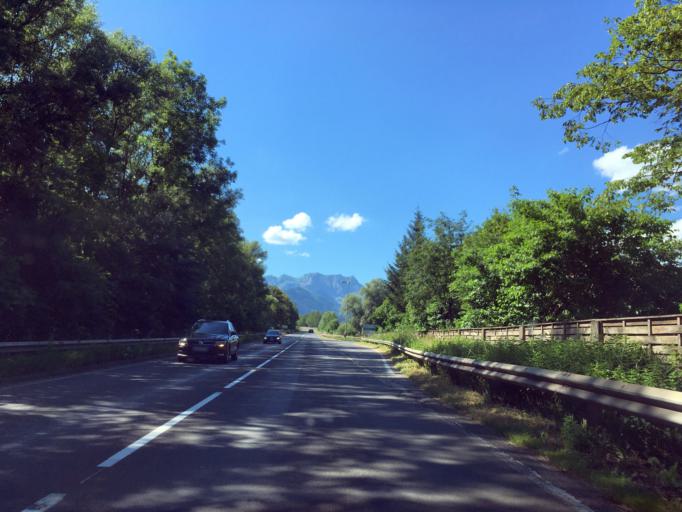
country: AT
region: Styria
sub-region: Politischer Bezirk Leoben
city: Sankt Peter-Freienstein
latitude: 47.4072
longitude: 15.0281
